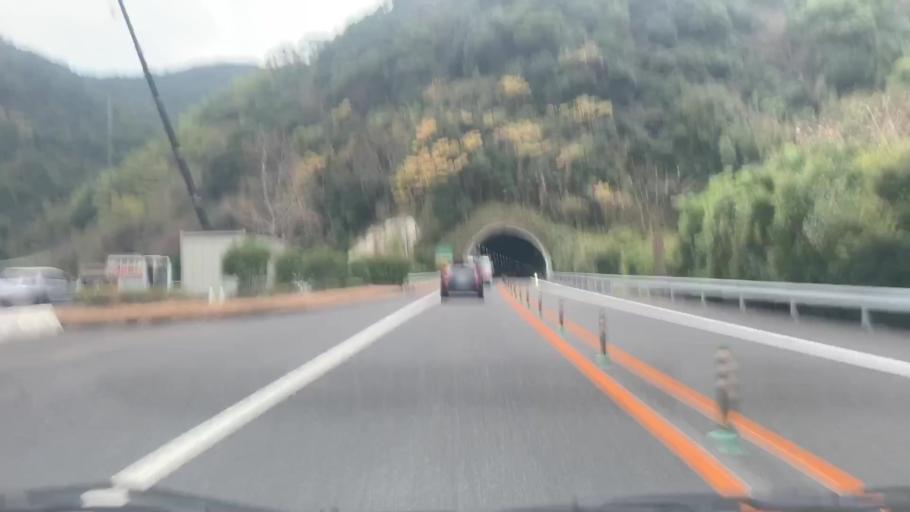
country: JP
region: Nagasaki
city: Nagasaki-shi
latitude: 32.7518
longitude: 129.9273
